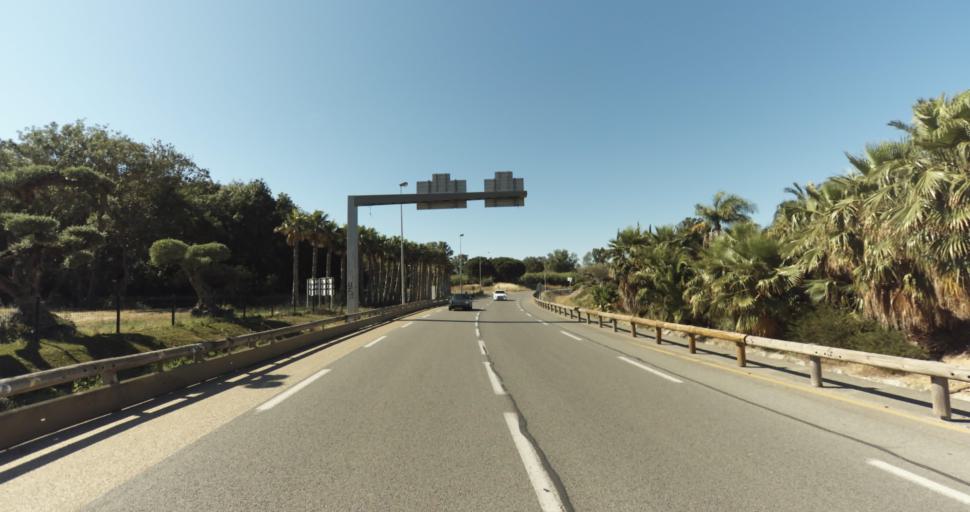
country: FR
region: Provence-Alpes-Cote d'Azur
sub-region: Departement du Var
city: Gassin
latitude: 43.2581
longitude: 6.5926
